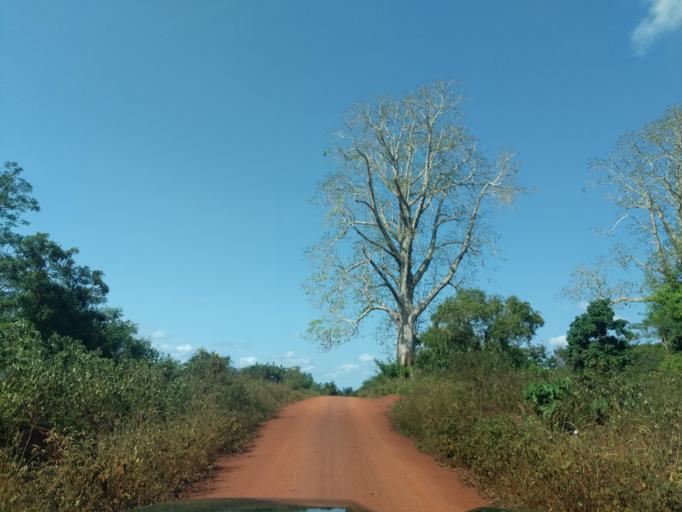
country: TZ
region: Tanga
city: Muheza
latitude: -5.3747
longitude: 38.5808
